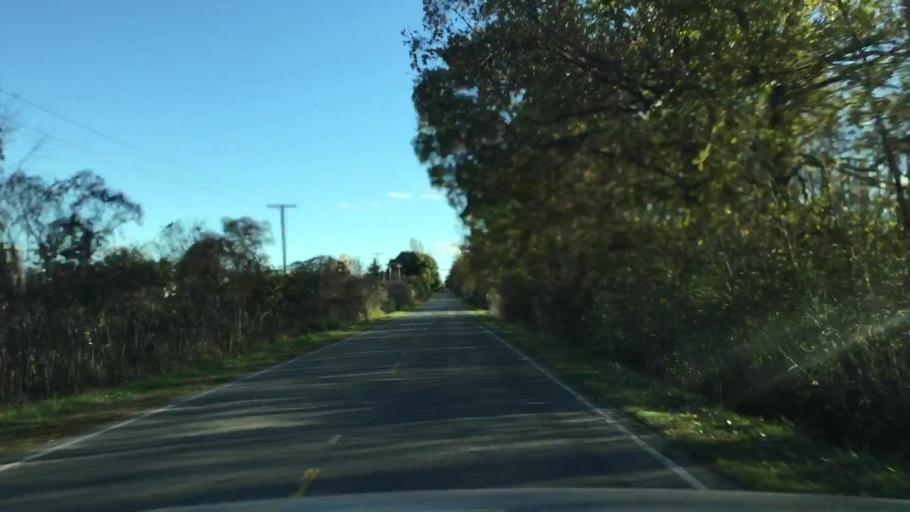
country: US
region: Michigan
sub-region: Lapeer County
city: Imlay City
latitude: 43.0002
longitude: -83.1840
